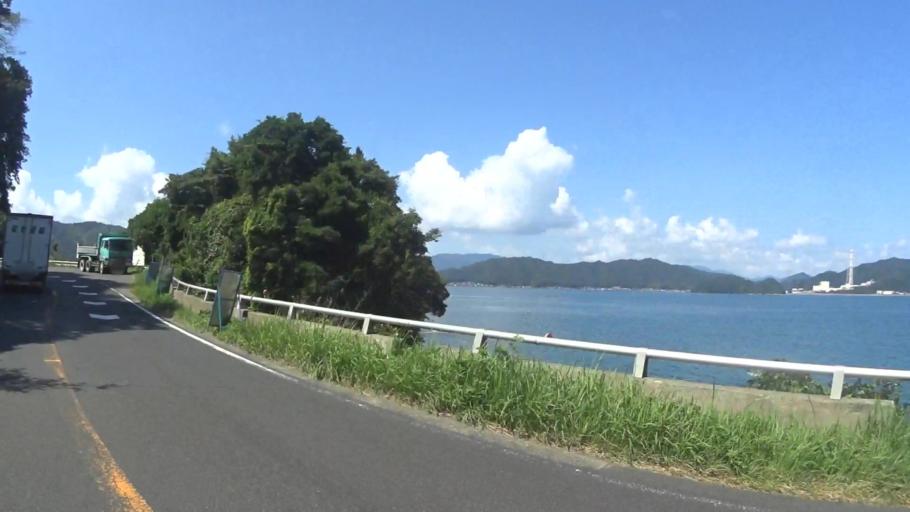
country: JP
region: Kyoto
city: Miyazu
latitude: 35.5344
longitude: 135.2565
